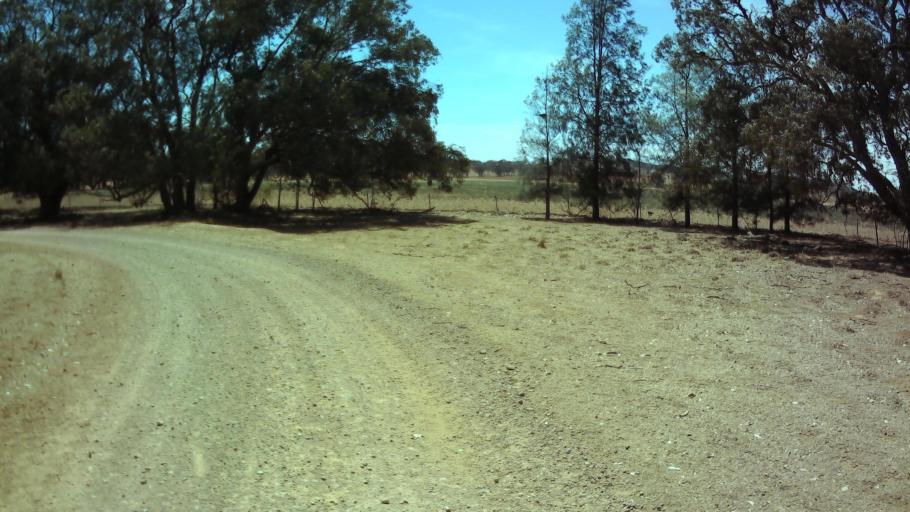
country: AU
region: New South Wales
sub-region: Weddin
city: Grenfell
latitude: -33.9822
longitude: 148.1652
